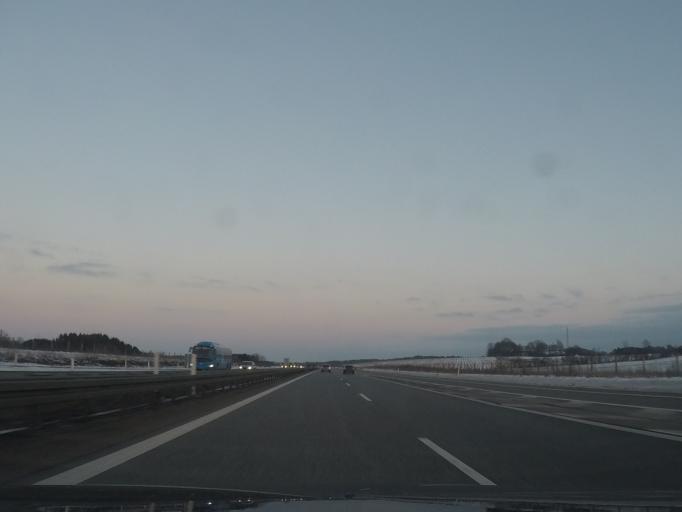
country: DK
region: Central Jutland
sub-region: Hedensted Kommune
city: Torring
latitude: 55.8542
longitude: 9.4273
